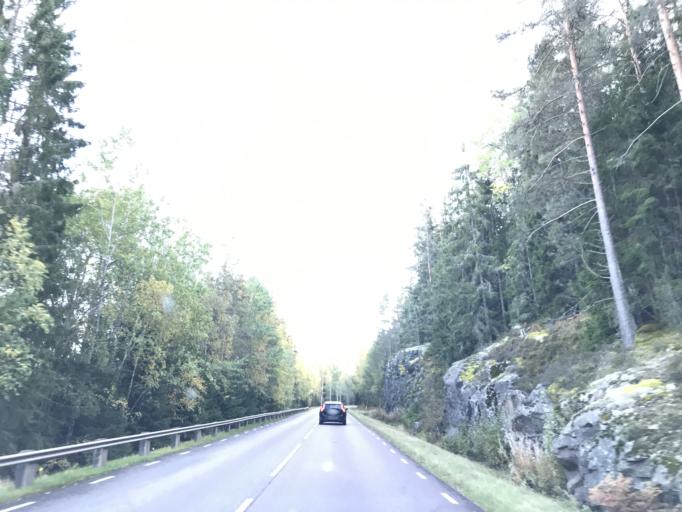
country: SE
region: Kalmar
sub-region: Hultsfreds Kommun
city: Virserum
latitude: 57.3923
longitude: 15.6059
